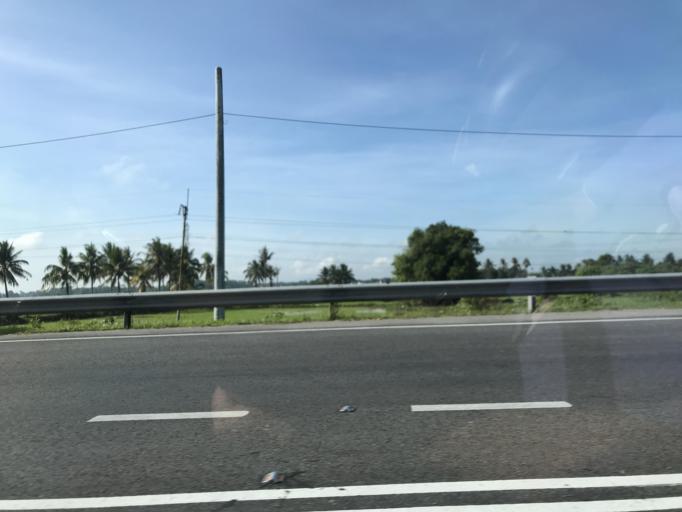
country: MY
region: Kelantan
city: Kampong Kadok
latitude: 6.0505
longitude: 102.2221
